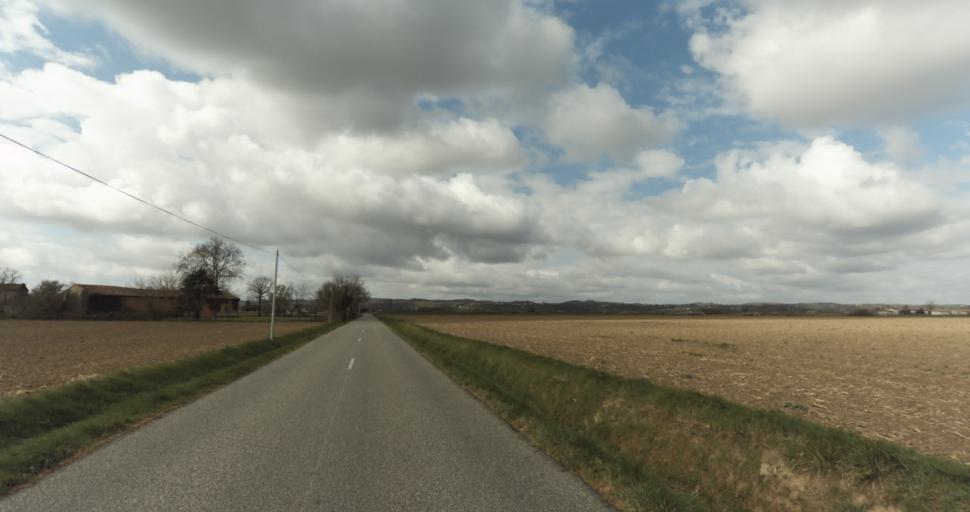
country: FR
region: Midi-Pyrenees
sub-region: Departement de la Haute-Garonne
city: Auterive
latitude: 43.3403
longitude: 1.4629
